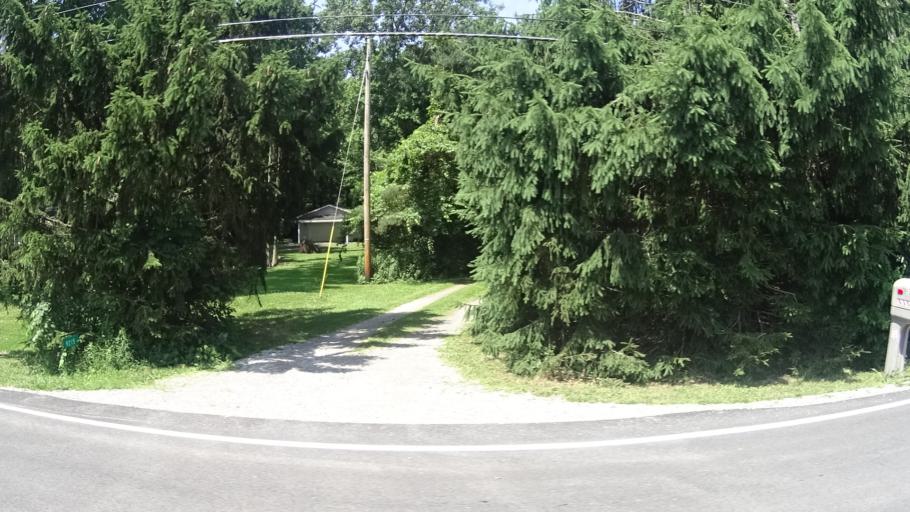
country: US
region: Ohio
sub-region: Lorain County
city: Vermilion
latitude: 41.3550
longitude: -82.4332
